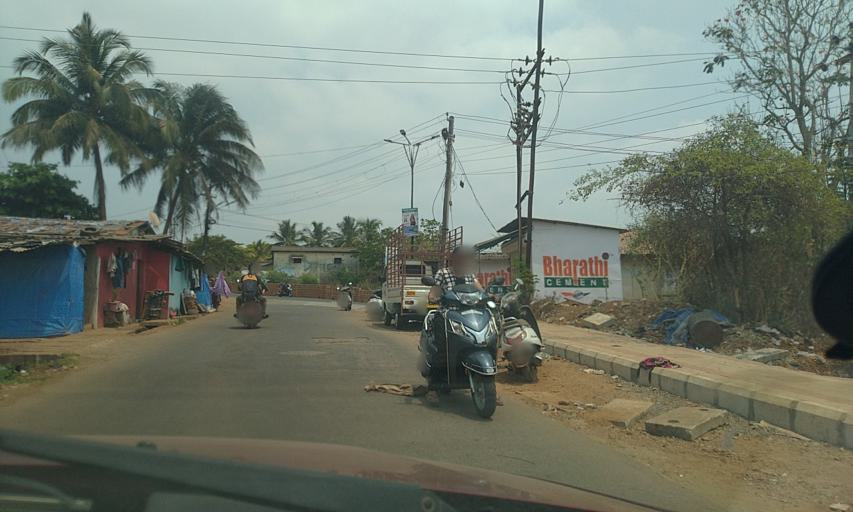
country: IN
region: Goa
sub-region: North Goa
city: Mapuca
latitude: 15.5969
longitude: 73.8099
